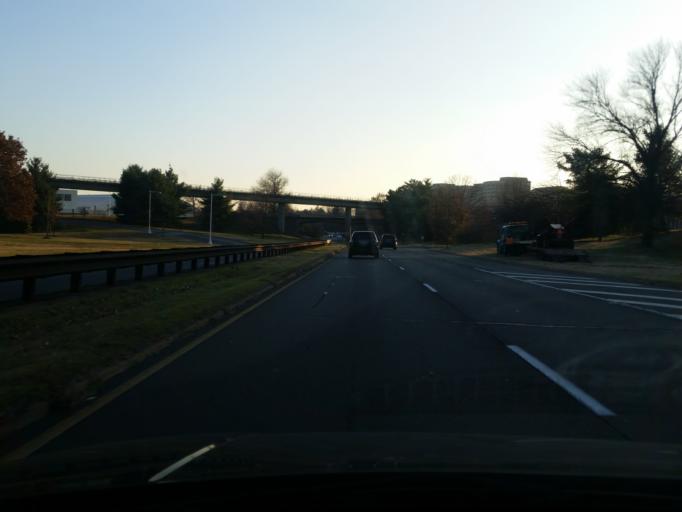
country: US
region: Virginia
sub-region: City of Alexandria
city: Alexandria
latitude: 38.8491
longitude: -77.0482
